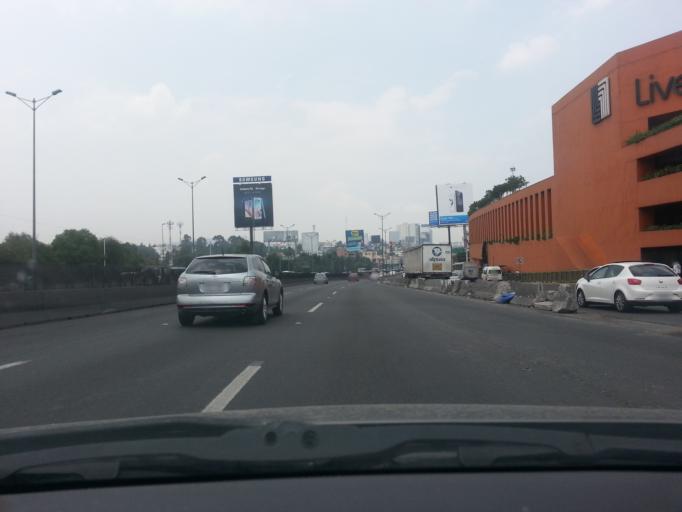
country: MX
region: Mexico
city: Vista Hermosa
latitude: 19.5113
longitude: -99.2358
